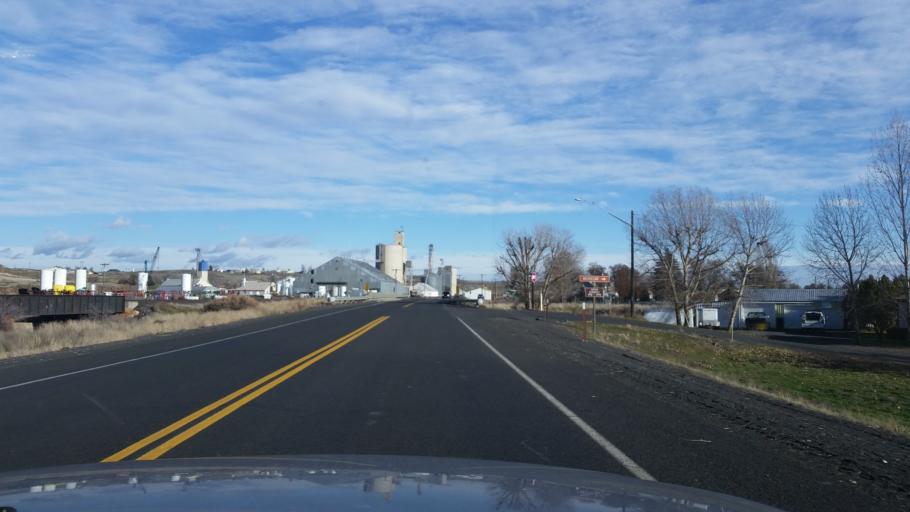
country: US
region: Washington
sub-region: Adams County
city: Ritzville
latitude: 47.3323
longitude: -118.6999
